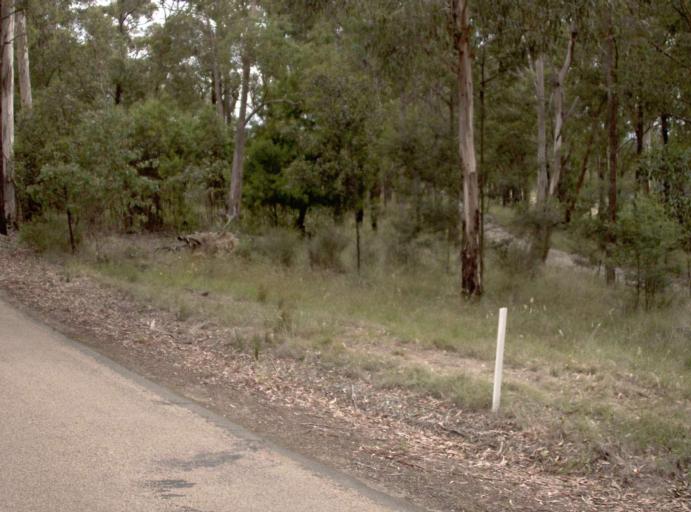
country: AU
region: Victoria
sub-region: East Gippsland
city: Bairnsdale
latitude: -37.7146
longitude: 147.5916
